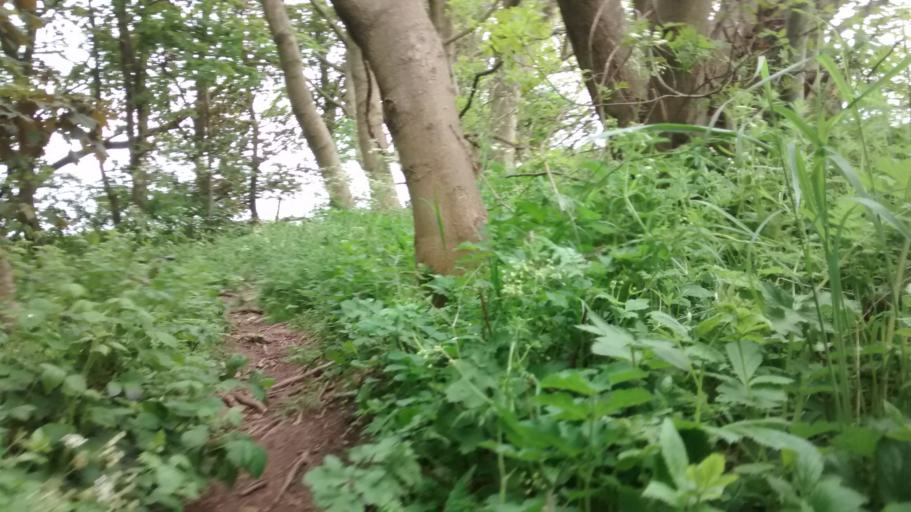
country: GB
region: England
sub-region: County Durham
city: Pittington
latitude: 54.7952
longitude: -1.4814
